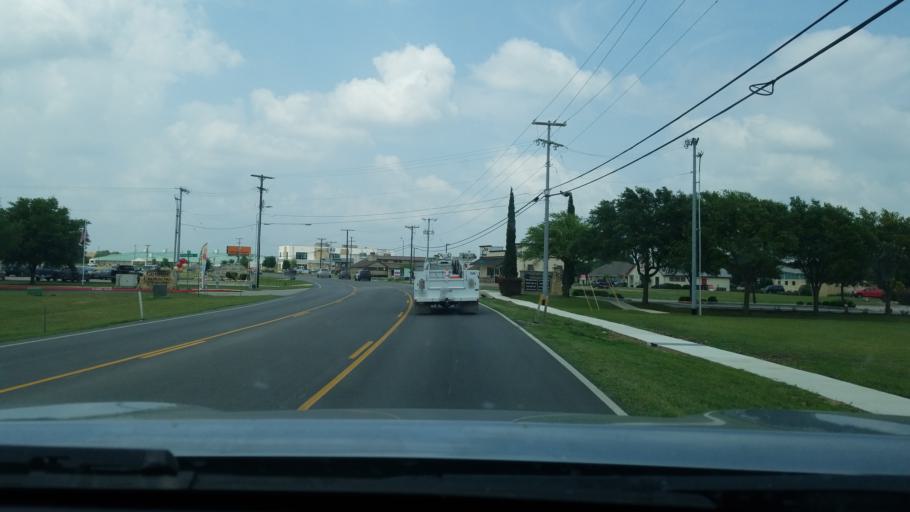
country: US
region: Texas
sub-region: Comal County
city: New Braunfels
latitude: 29.7254
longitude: -98.0957
